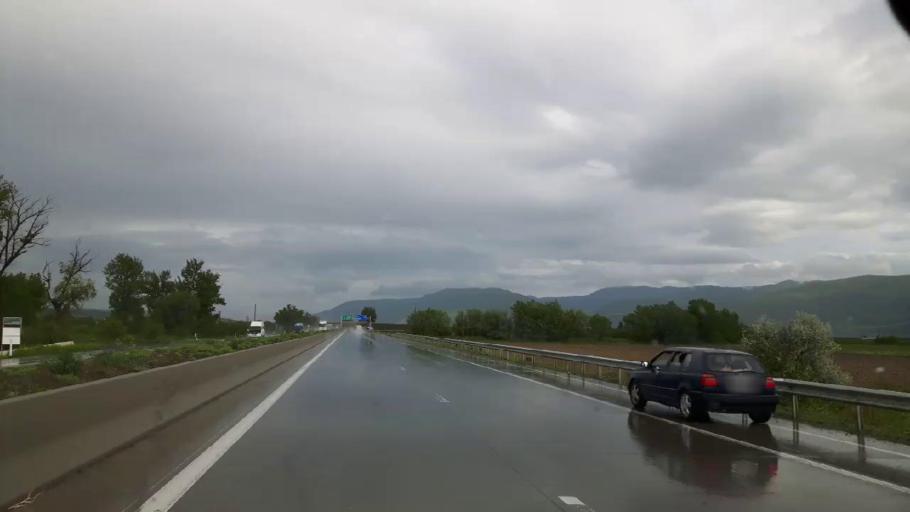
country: GE
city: Agara
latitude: 42.0348
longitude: 43.9419
